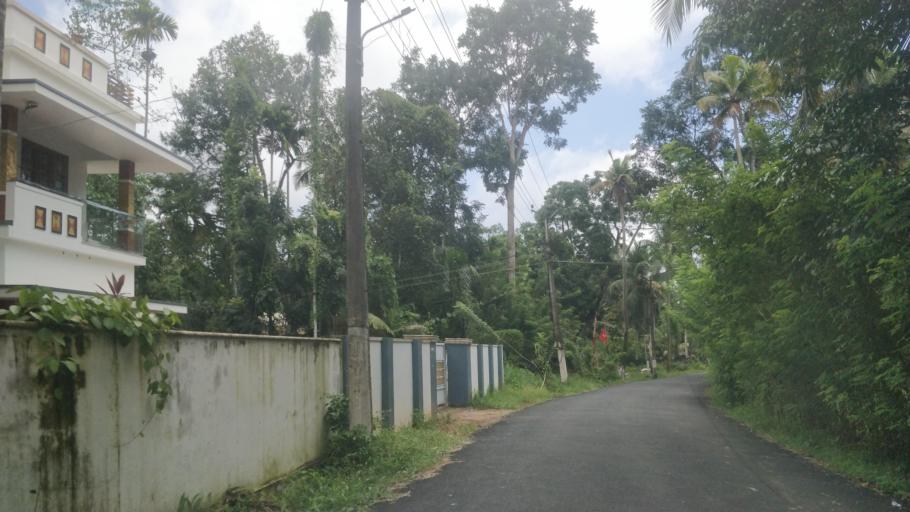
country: IN
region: Kerala
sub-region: Alappuzha
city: Shertallai
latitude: 9.6591
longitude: 76.3716
